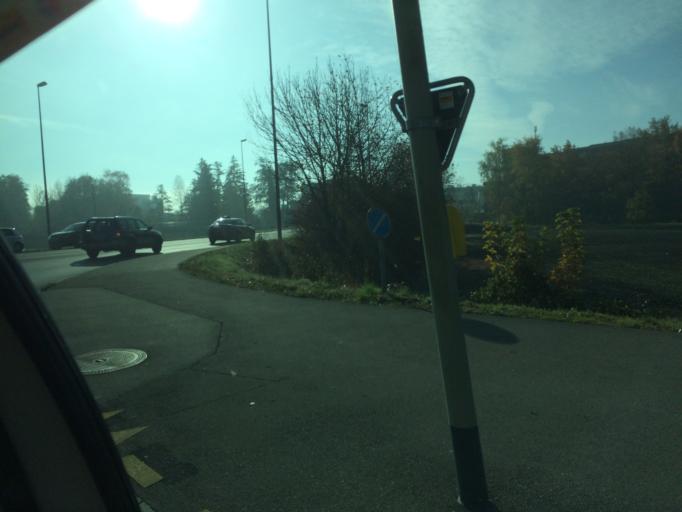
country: CH
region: Zurich
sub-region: Bezirk Uster
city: Duebendorf / Wasserfurren
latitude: 47.4027
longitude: 8.6058
